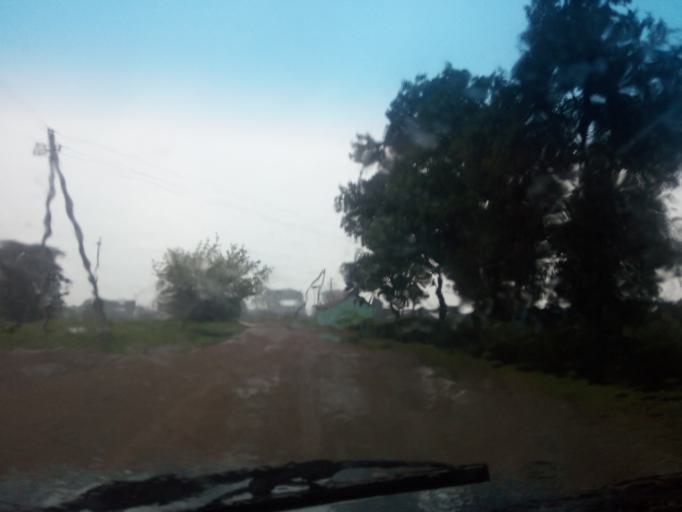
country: BY
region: Vitebsk
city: Dzisna
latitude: 55.6701
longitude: 28.3256
